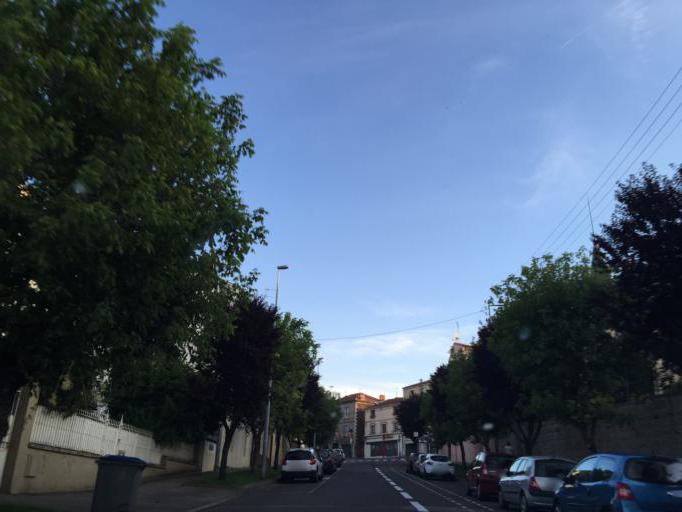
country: FR
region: Rhone-Alpes
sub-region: Departement de la Loire
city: Saint-Chamond
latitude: 45.4708
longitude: 4.5150
